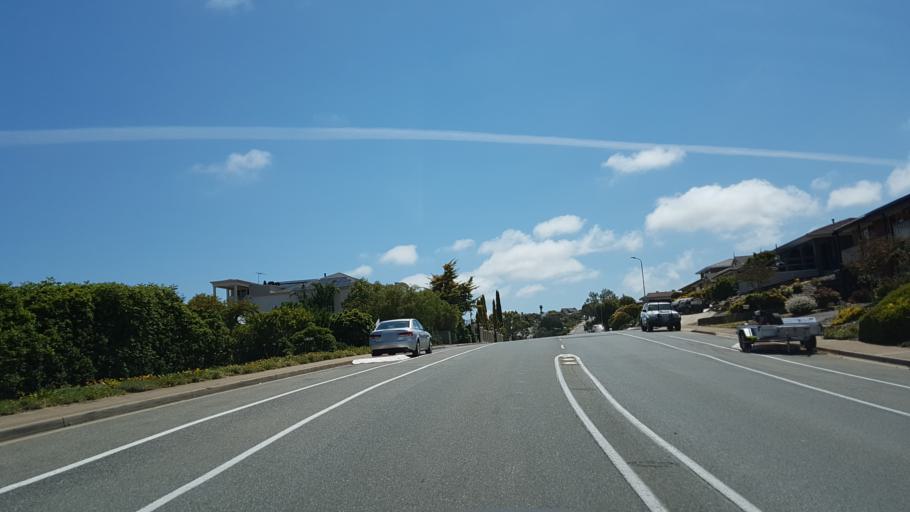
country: AU
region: South Australia
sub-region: Marion
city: Marino
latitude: -35.0666
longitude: 138.5067
